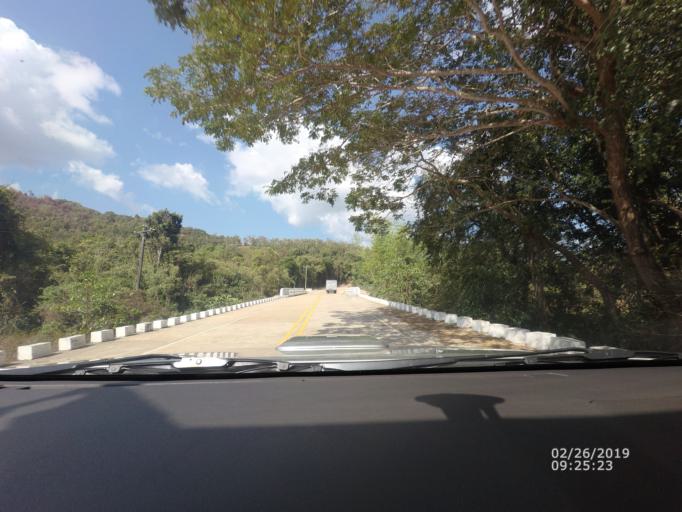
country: PH
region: Mimaropa
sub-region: Province of Palawan
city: Salvacion
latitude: 12.0342
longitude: 120.0403
